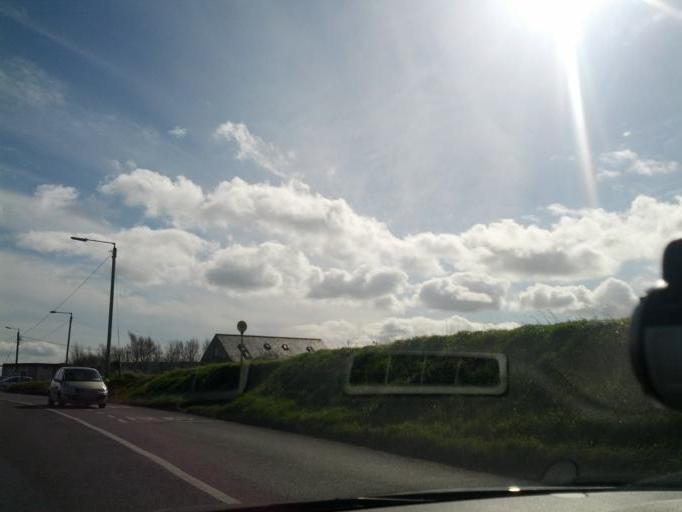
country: IE
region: Leinster
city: Portmarnock
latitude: 53.4102
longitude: -6.1368
